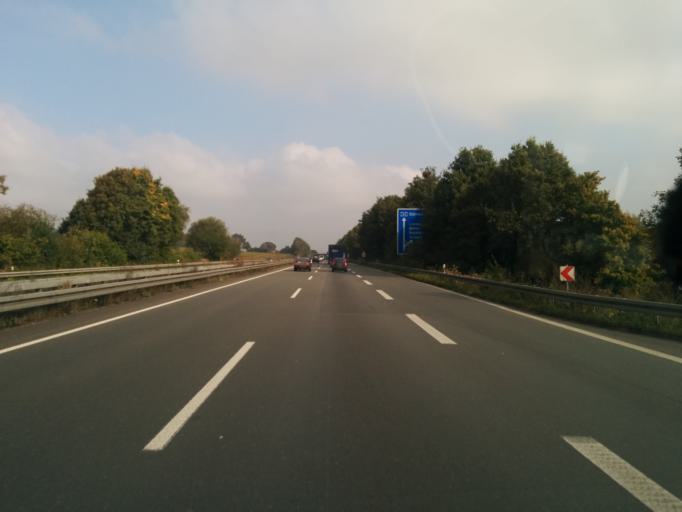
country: DE
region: North Rhine-Westphalia
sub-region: Regierungsbezirk Munster
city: Haltern
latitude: 51.7736
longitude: 7.1764
